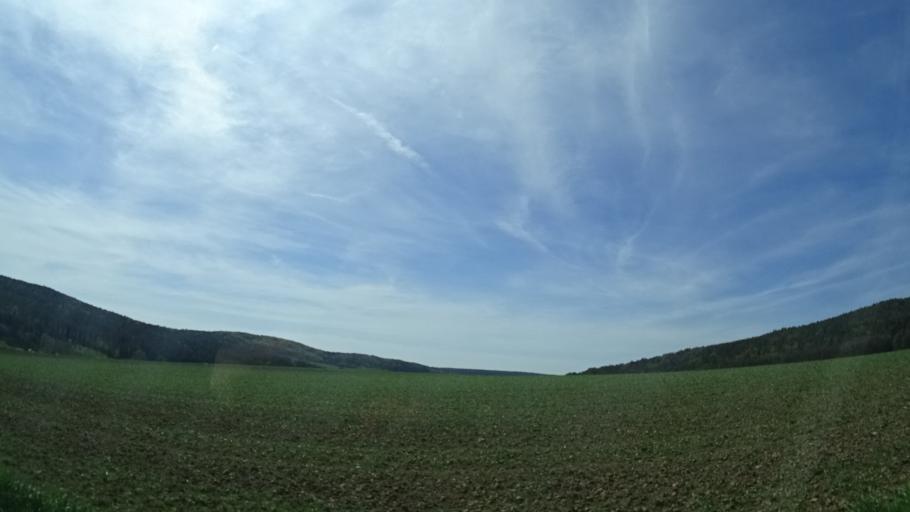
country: DE
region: Bavaria
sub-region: Regierungsbezirk Unterfranken
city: Burgpreppach
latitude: 50.1574
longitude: 10.6354
